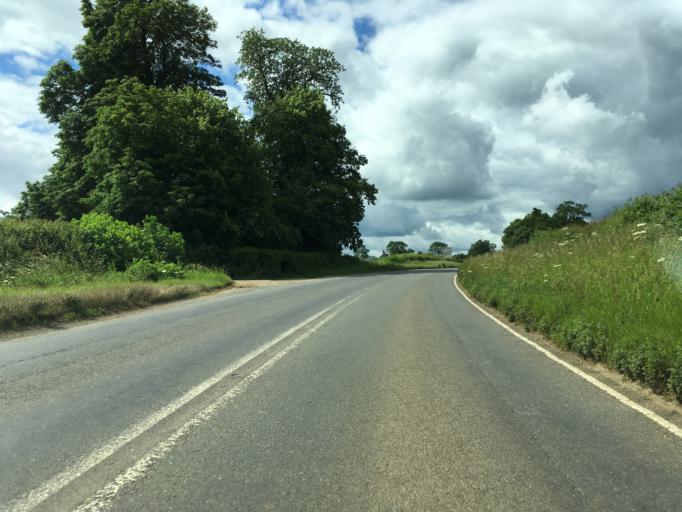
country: GB
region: England
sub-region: Oxfordshire
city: Bloxham
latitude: 52.0120
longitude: -1.3828
